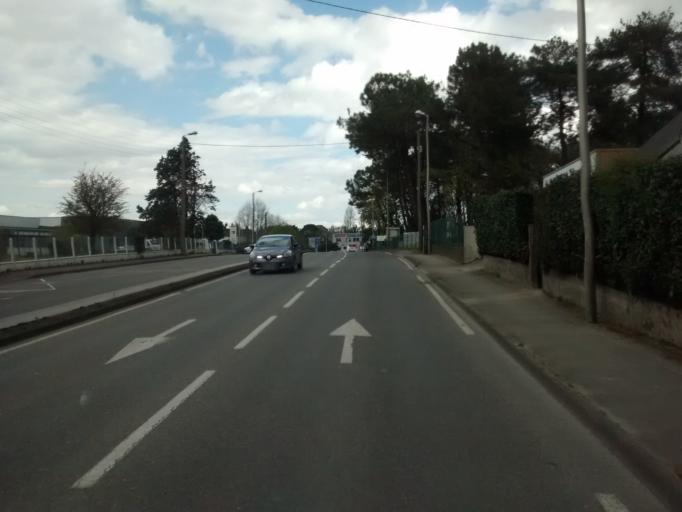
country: FR
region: Brittany
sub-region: Departement du Morbihan
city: Vannes
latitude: 47.6581
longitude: -2.7191
